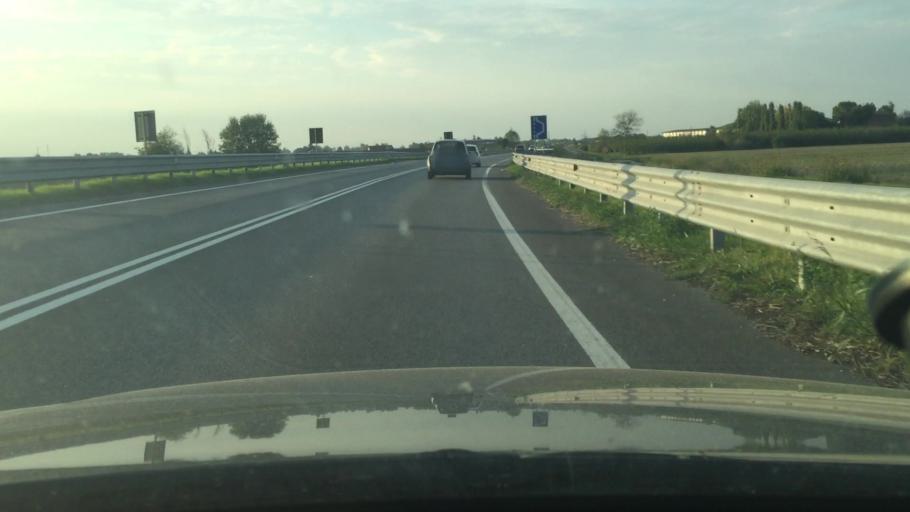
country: IT
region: Emilia-Romagna
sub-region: Provincia di Ferrara
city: Ferrara
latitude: 44.8276
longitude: 11.5824
